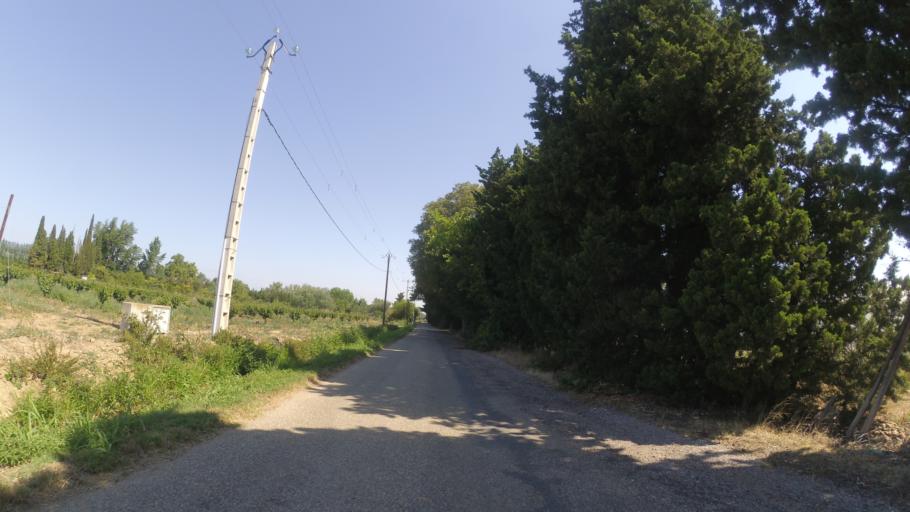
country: FR
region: Languedoc-Roussillon
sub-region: Departement des Pyrenees-Orientales
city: Corneilla-la-Riviere
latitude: 42.6718
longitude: 2.7323
